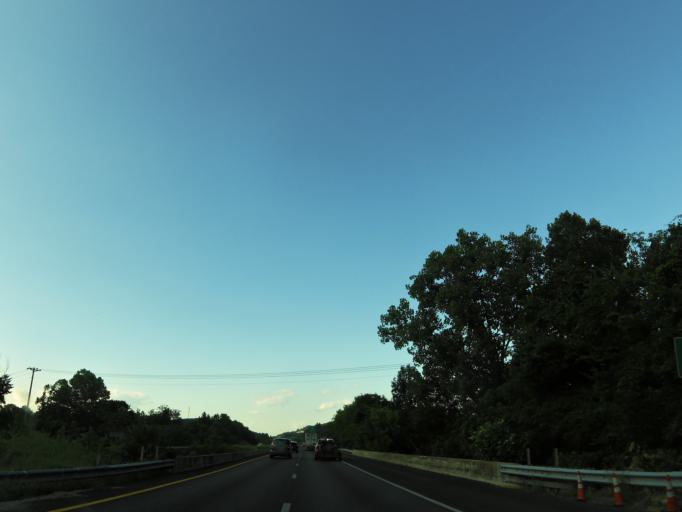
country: US
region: Tennessee
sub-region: Williamson County
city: Thompson's Station
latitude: 35.8051
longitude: -86.8504
